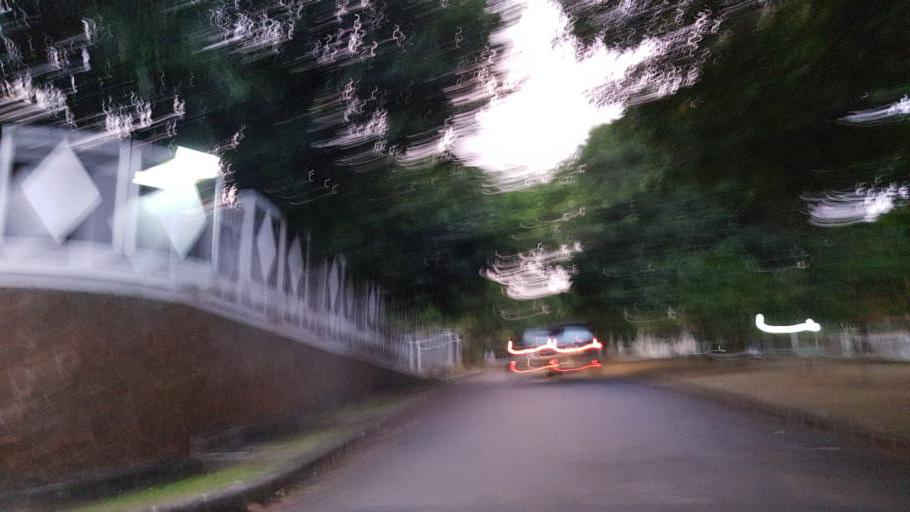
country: ID
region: West Java
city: Pamulang
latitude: -6.3432
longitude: 106.7811
